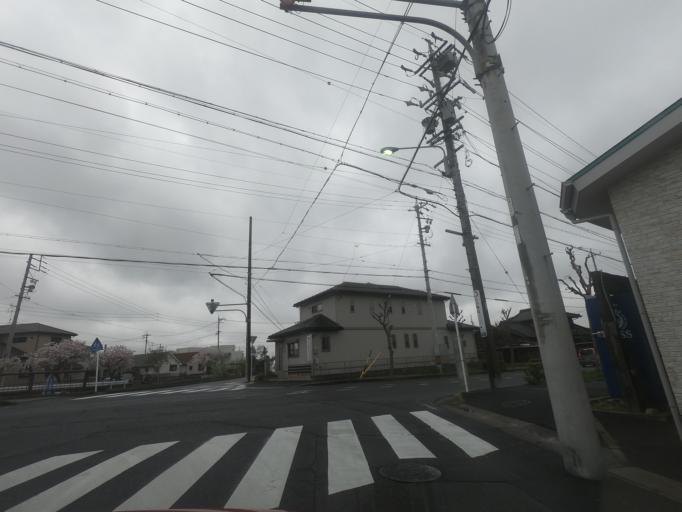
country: JP
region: Aichi
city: Kasugai
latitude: 35.2638
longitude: 136.9543
